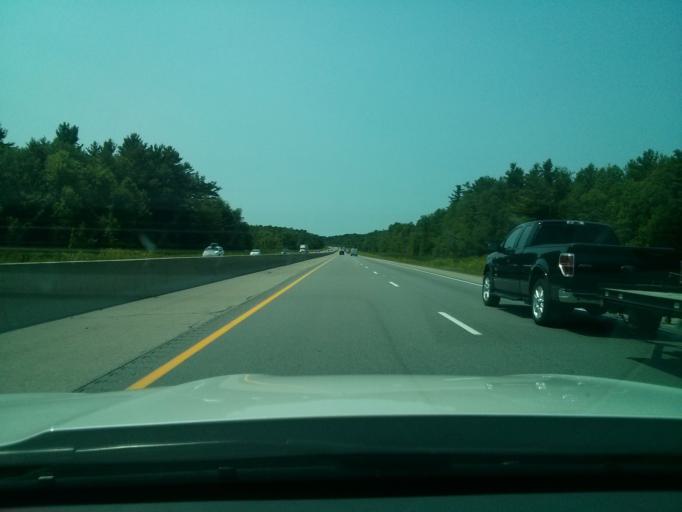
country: CA
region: Ontario
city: Brockville
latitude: 44.5607
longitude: -75.7501
